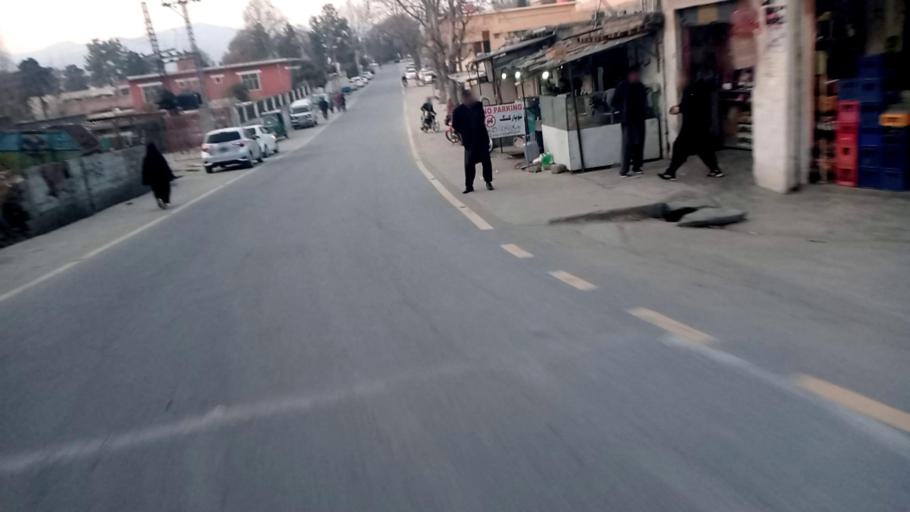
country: PK
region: Khyber Pakhtunkhwa
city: Saidu Sharif
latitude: 34.7578
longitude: 72.3602
